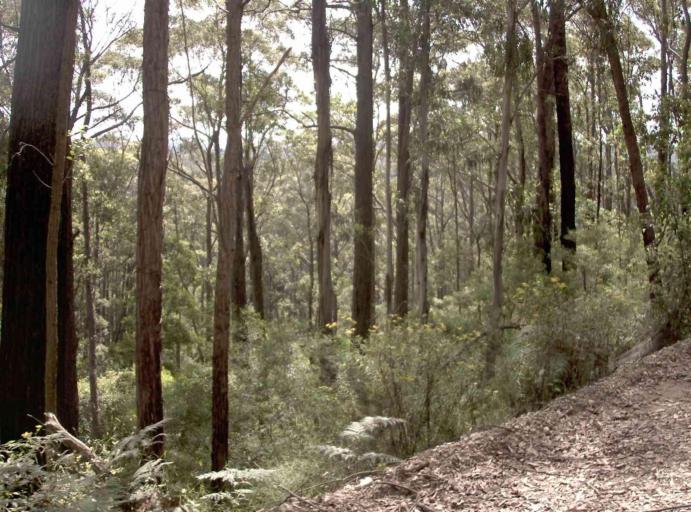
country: AU
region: Victoria
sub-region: East Gippsland
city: Lakes Entrance
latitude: -37.6166
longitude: 148.6993
